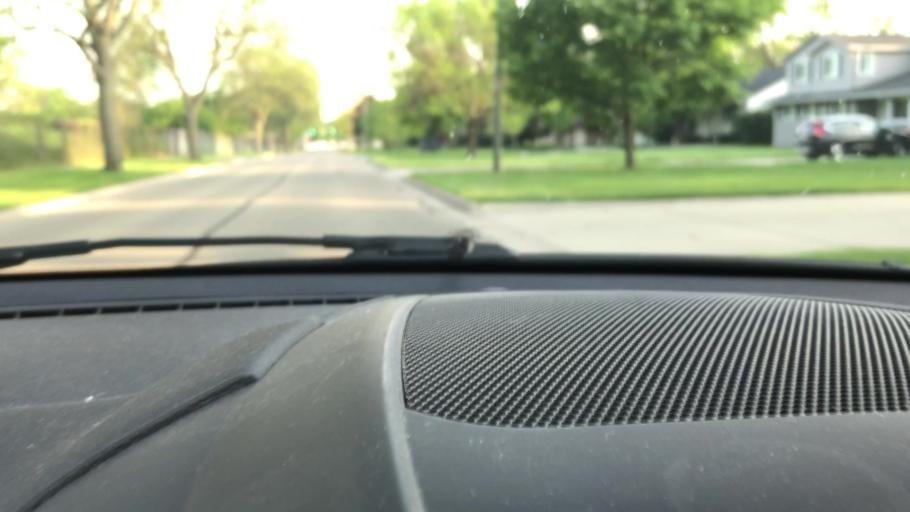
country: US
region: Michigan
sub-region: Oakland County
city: Huntington Woods
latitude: 42.4776
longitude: -83.1729
